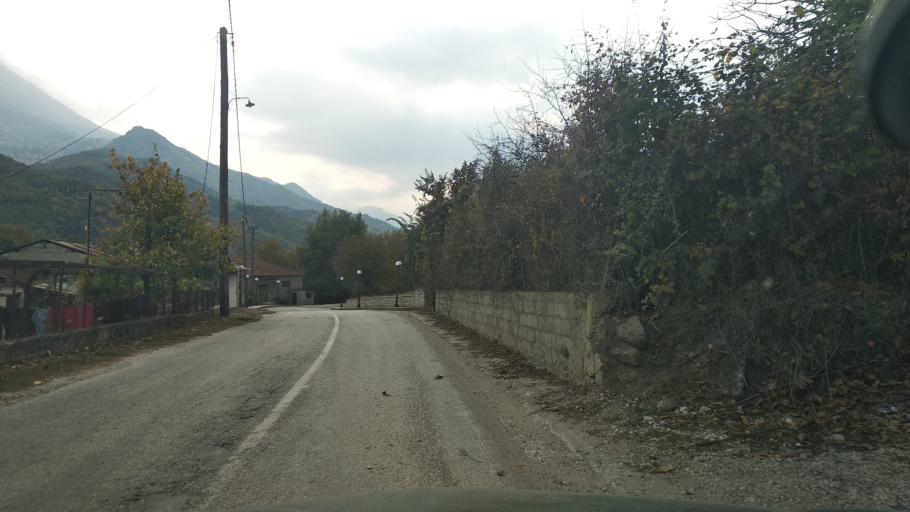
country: GR
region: Thessaly
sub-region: Trikala
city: Kastraki
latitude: 39.6920
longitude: 21.5186
